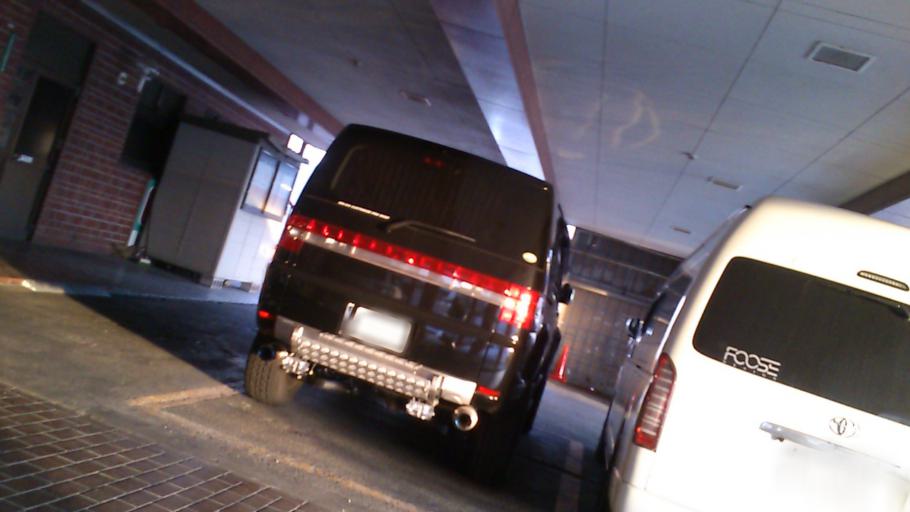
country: JP
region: Aomori
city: Hirosaki
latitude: 40.6018
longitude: 140.4829
